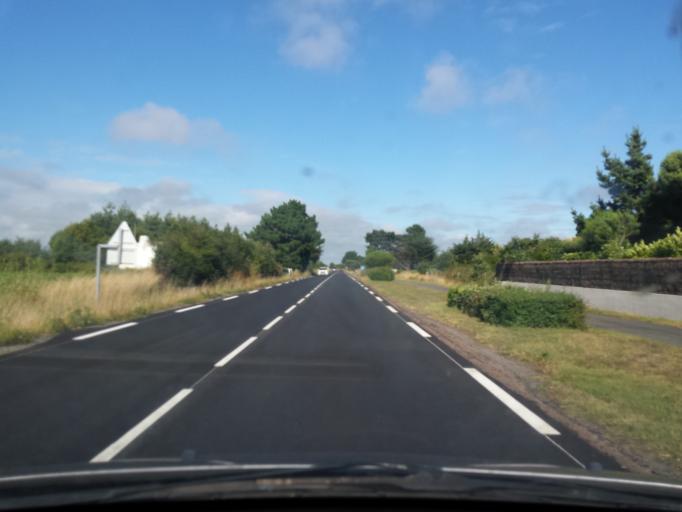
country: FR
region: Pays de la Loire
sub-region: Departement de la Vendee
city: Bretignolles-sur-Mer
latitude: 46.6350
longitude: -1.8329
